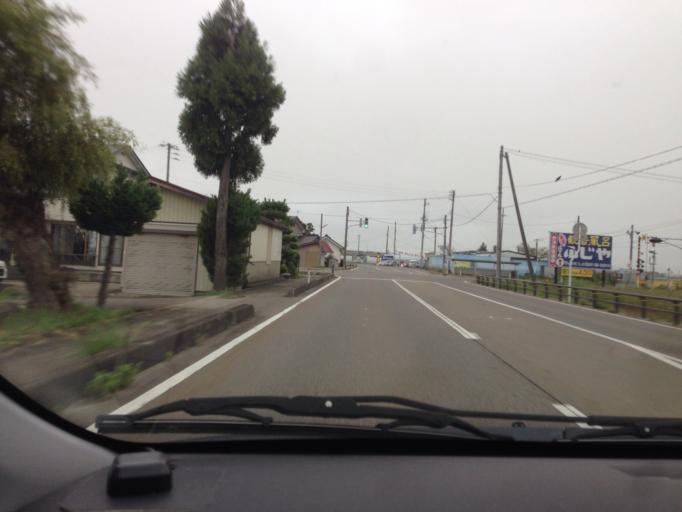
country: JP
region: Fukushima
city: Kitakata
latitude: 37.5780
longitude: 139.8959
